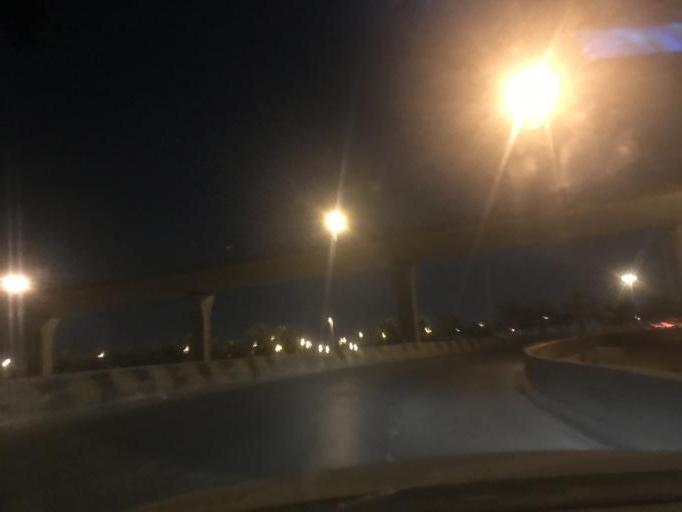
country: SA
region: Ar Riyad
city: Riyadh
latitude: 24.8297
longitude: 46.7200
